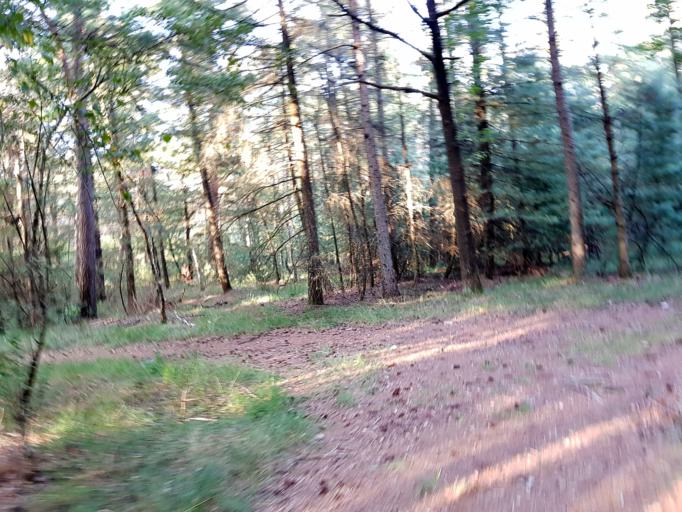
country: NL
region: Utrecht
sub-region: Gemeente Utrechtse Heuvelrug
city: Maarsbergen
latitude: 52.0476
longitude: 5.4357
